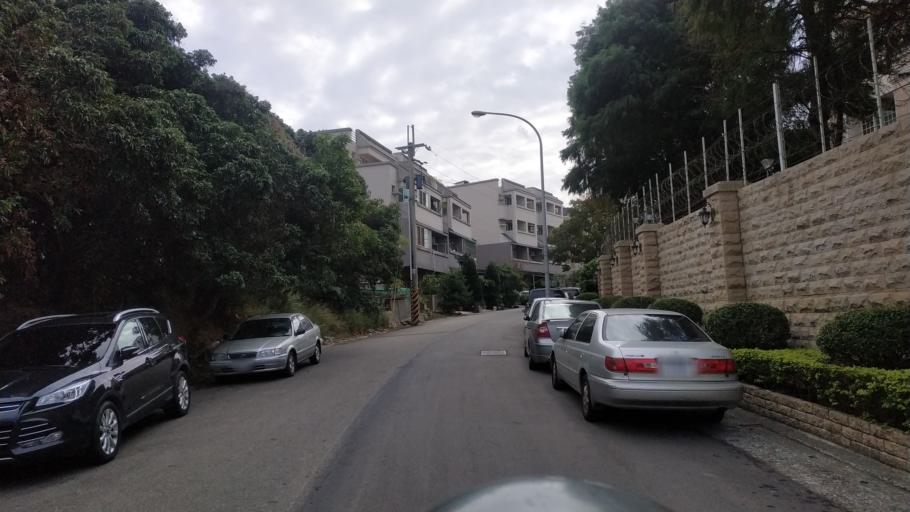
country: TW
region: Taiwan
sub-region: Taichung City
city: Taichung
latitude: 24.2138
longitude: 120.5767
